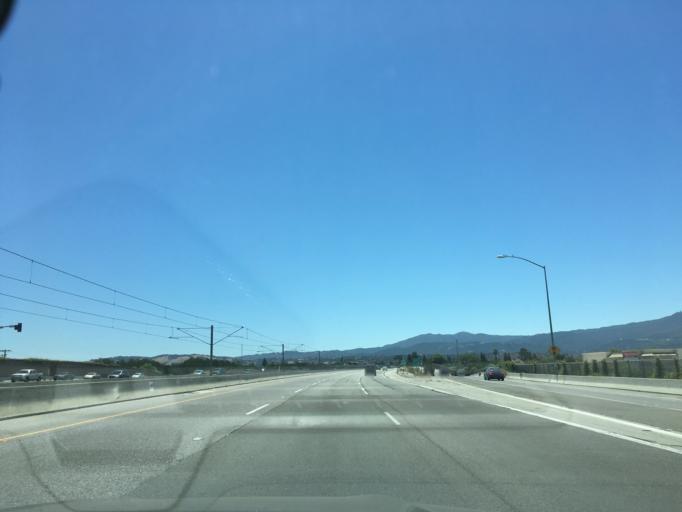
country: US
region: California
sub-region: Santa Clara County
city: Seven Trees
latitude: 37.2778
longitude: -121.8643
